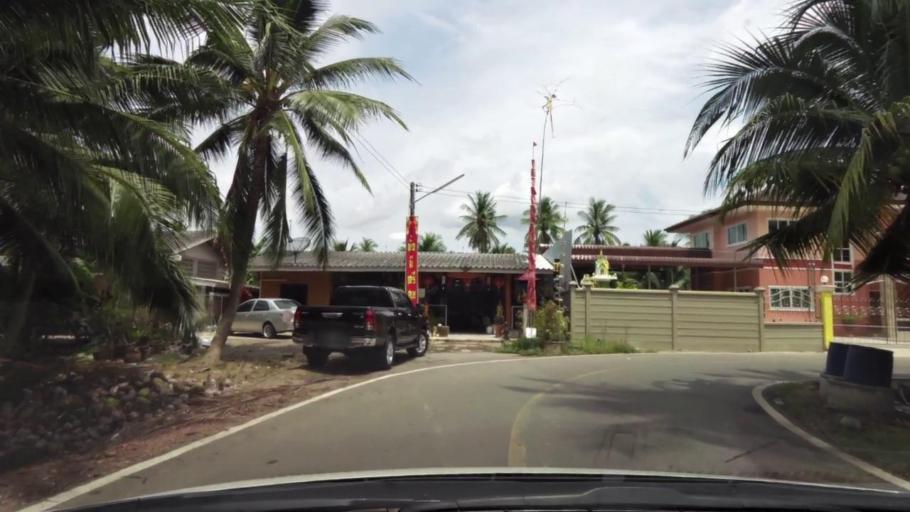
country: TH
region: Ratchaburi
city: Damnoen Saduak
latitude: 13.5171
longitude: 100.0106
